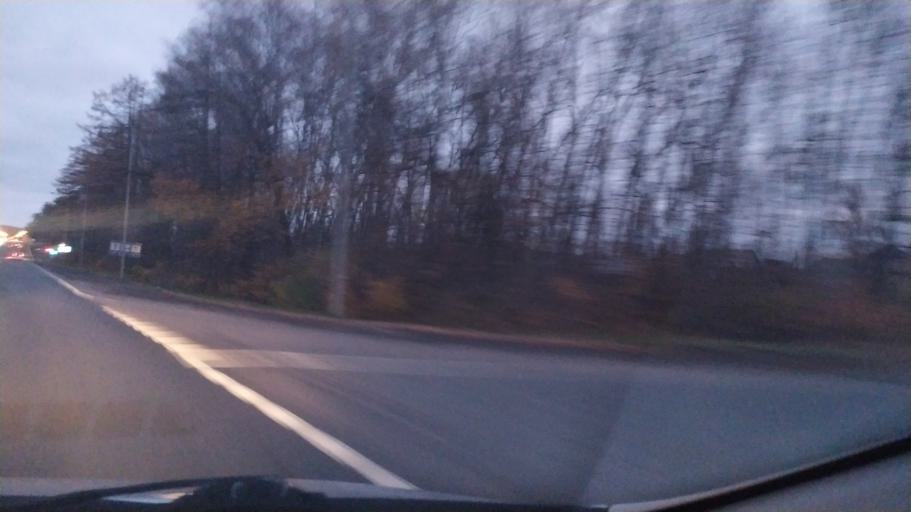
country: RU
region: Chuvashia
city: Kugesi
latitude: 56.0274
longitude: 47.3049
